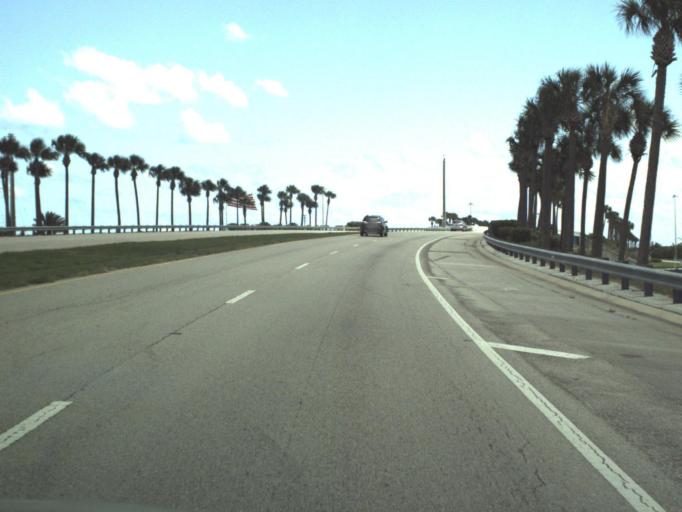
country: US
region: Florida
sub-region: Brevard County
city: Cape Canaveral
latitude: 28.4049
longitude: -80.6203
